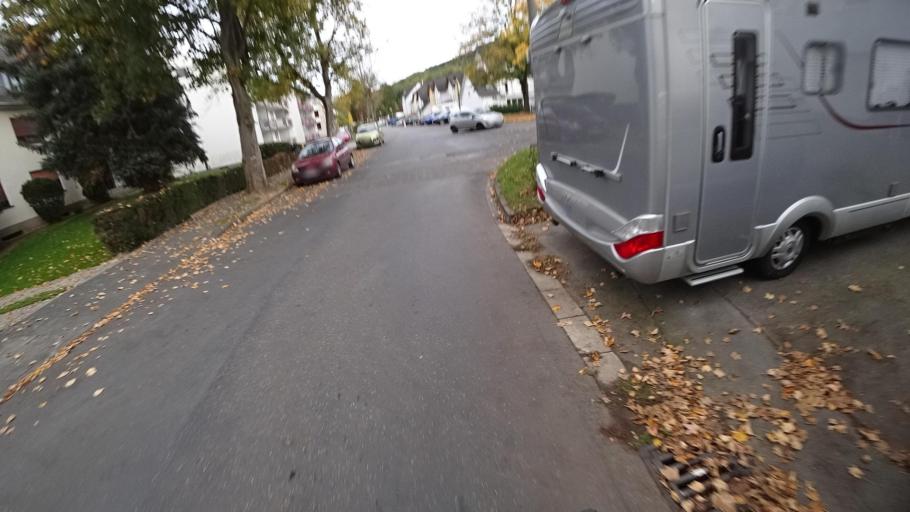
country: DE
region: Rheinland-Pfalz
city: Sinzig
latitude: 50.5490
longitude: 7.2148
